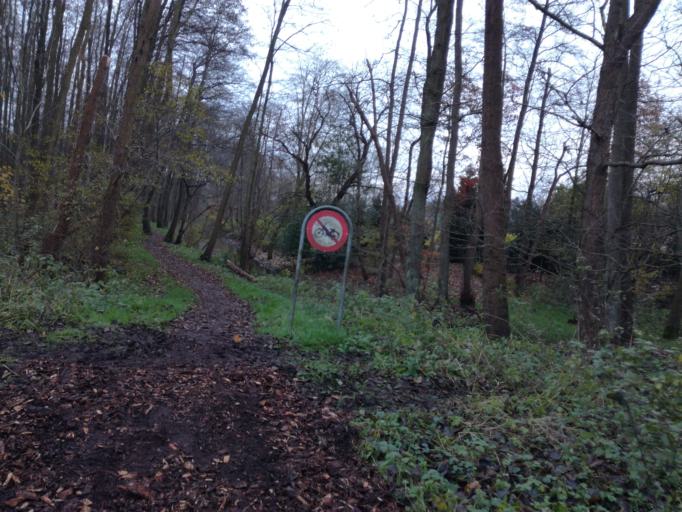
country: DK
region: South Denmark
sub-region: Vejle Kommune
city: Borkop
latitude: 55.6415
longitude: 9.6553
